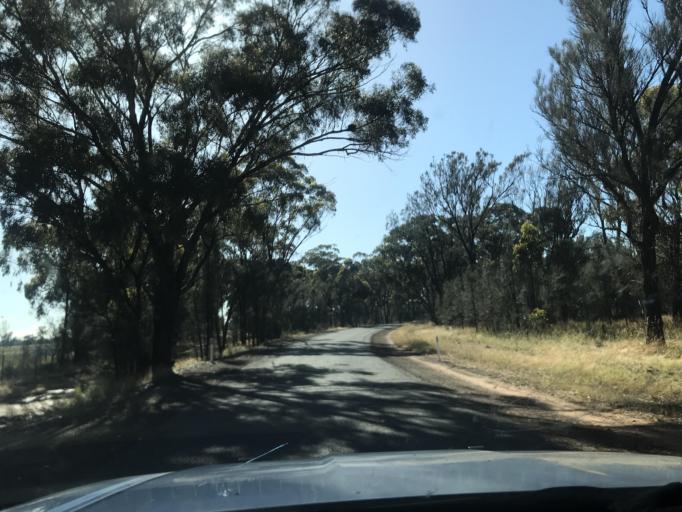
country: AU
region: Victoria
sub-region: Horsham
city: Horsham
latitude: -37.0087
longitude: 141.6581
